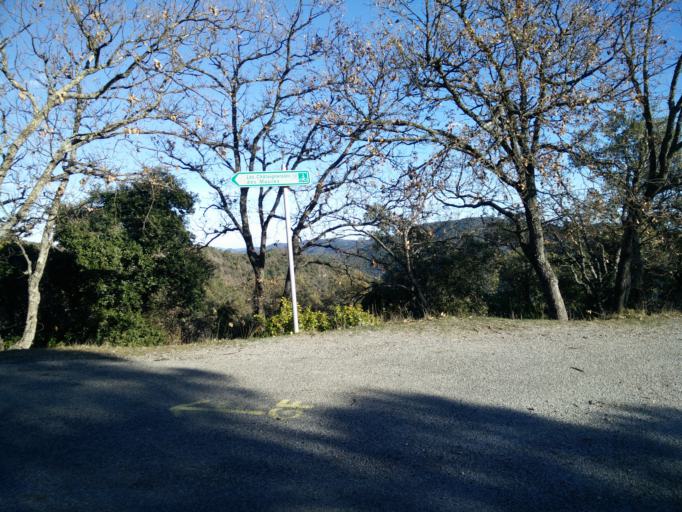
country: FR
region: Provence-Alpes-Cote d'Azur
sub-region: Departement du Var
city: Gonfaron
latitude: 43.2790
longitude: 6.2970
